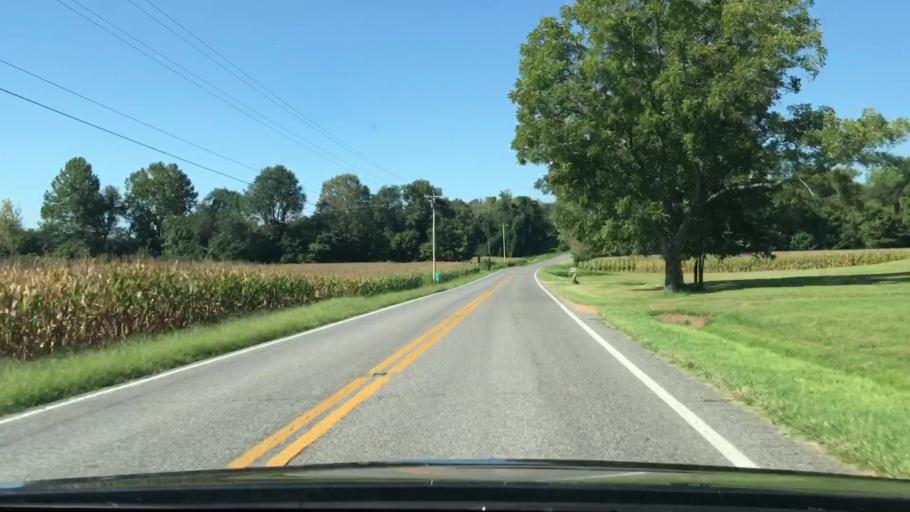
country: US
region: Kentucky
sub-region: Graves County
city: Mayfield
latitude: 36.7688
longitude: -88.5643
